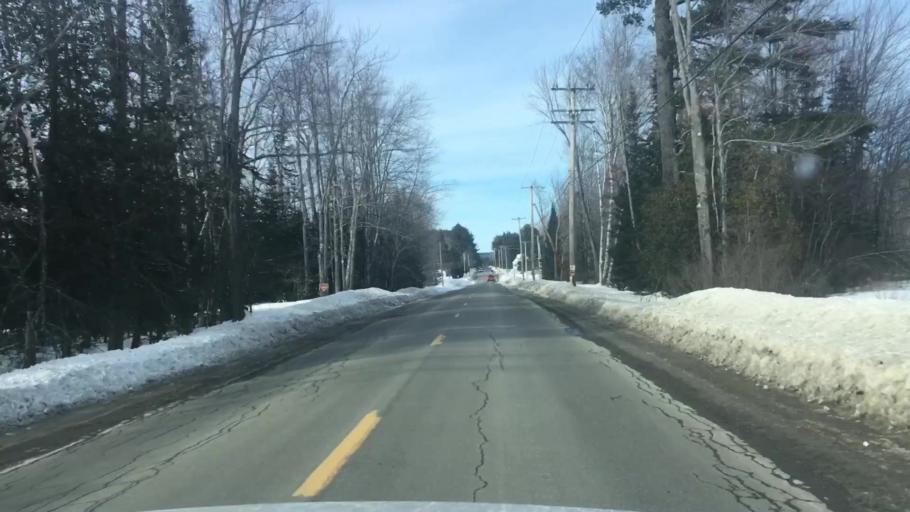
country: US
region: Maine
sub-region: Penobscot County
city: Charleston
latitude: 45.0495
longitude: -69.0296
